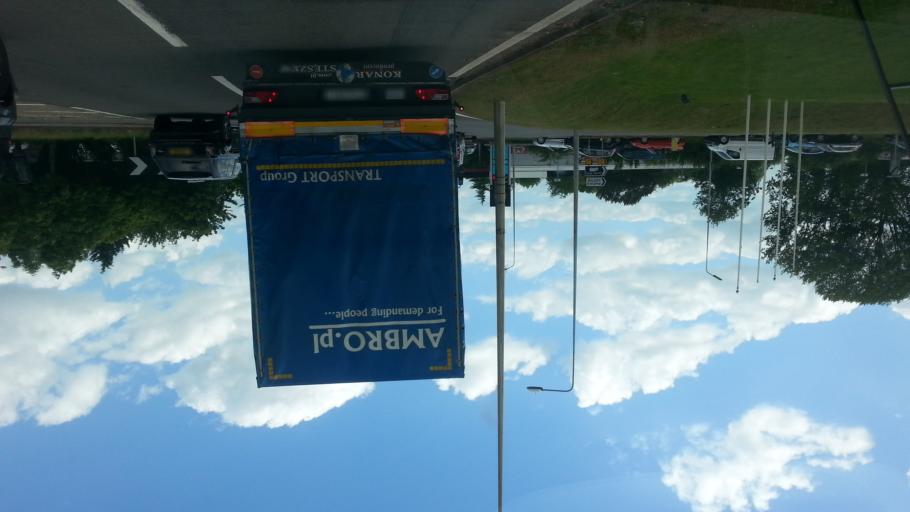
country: GB
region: England
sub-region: Central Bedfordshire
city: Sandy
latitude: 52.1271
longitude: -0.2991
